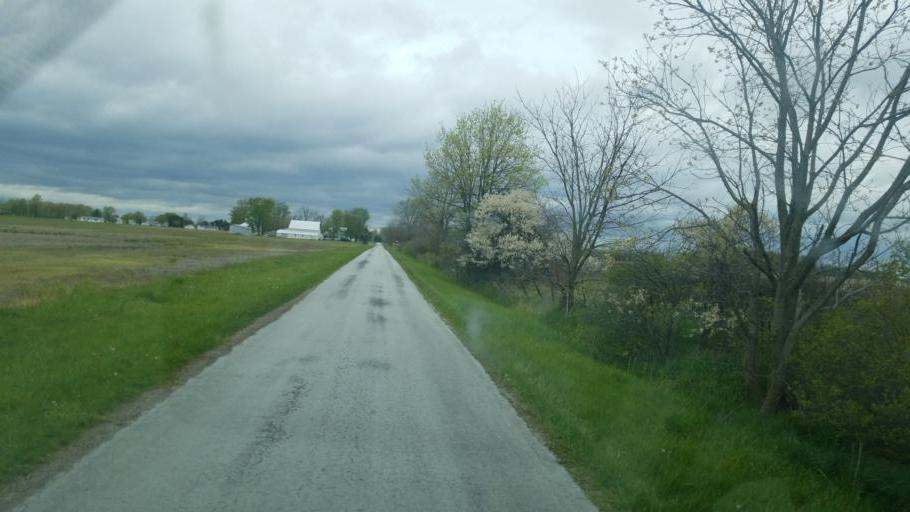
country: US
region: Ohio
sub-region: Marion County
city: Prospect
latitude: 40.5111
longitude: -83.2382
